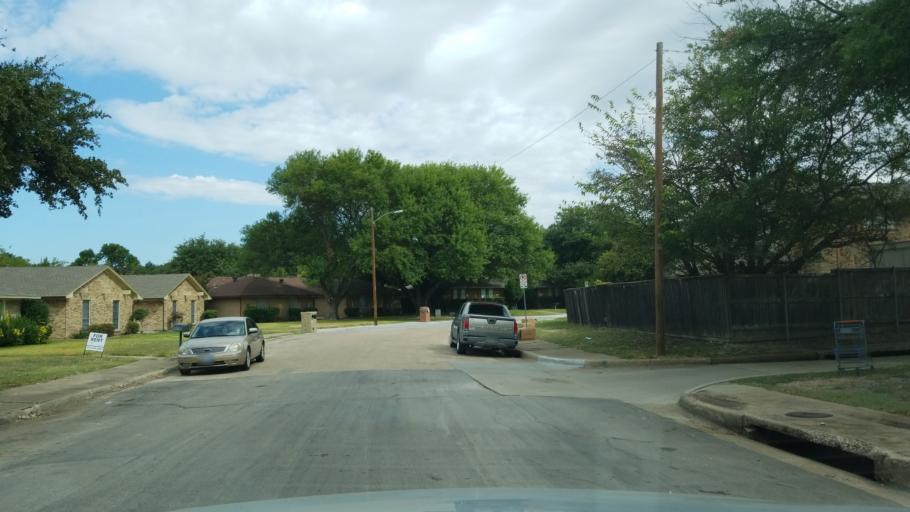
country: US
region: Texas
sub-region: Dallas County
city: Richardson
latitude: 32.9638
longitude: -96.7719
